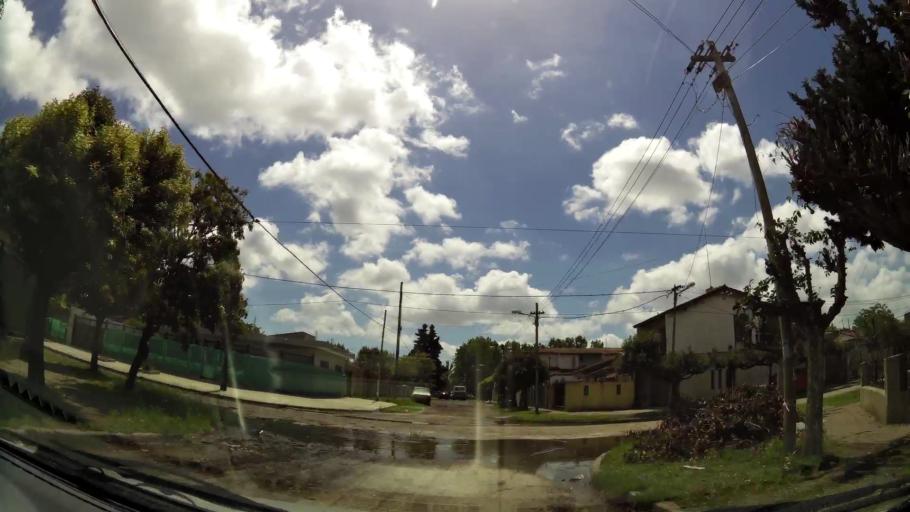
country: AR
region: Buenos Aires
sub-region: Partido de Quilmes
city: Quilmes
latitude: -34.8282
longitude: -58.2258
